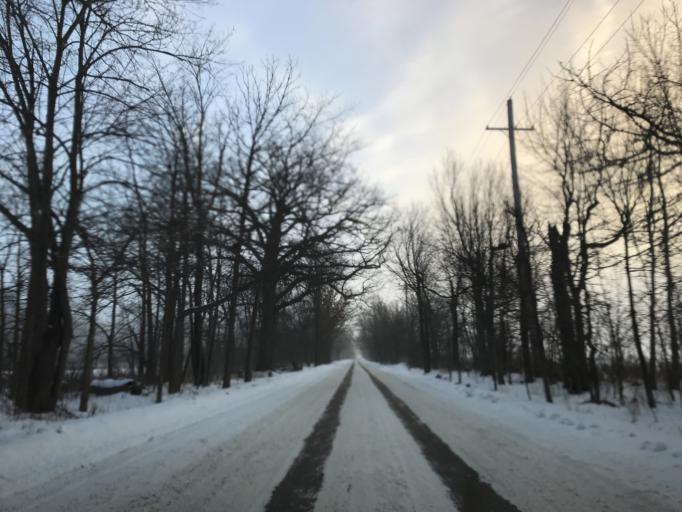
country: US
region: Michigan
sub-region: Oakland County
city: Wixom
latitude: 42.4919
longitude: -83.5891
